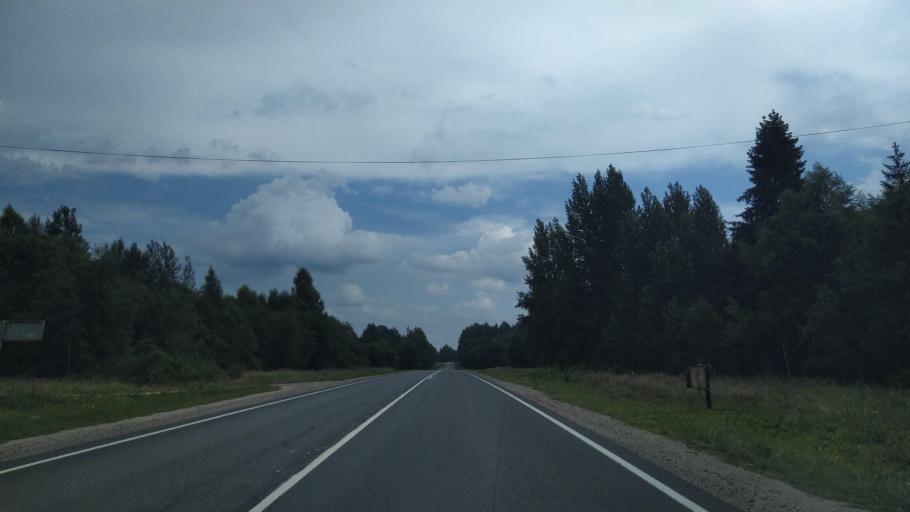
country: RU
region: Pskov
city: Pskov
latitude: 57.8140
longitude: 28.6716
